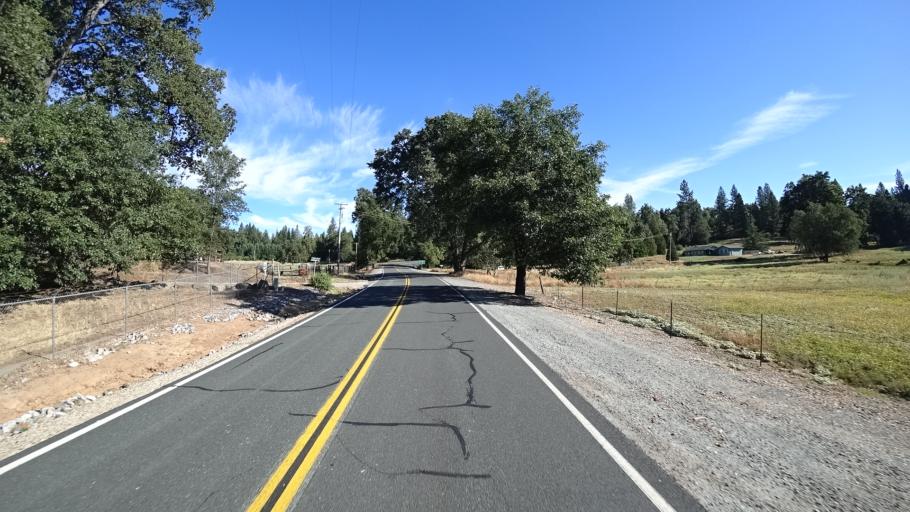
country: US
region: California
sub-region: Amador County
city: Pioneer
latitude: 38.3841
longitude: -120.5330
